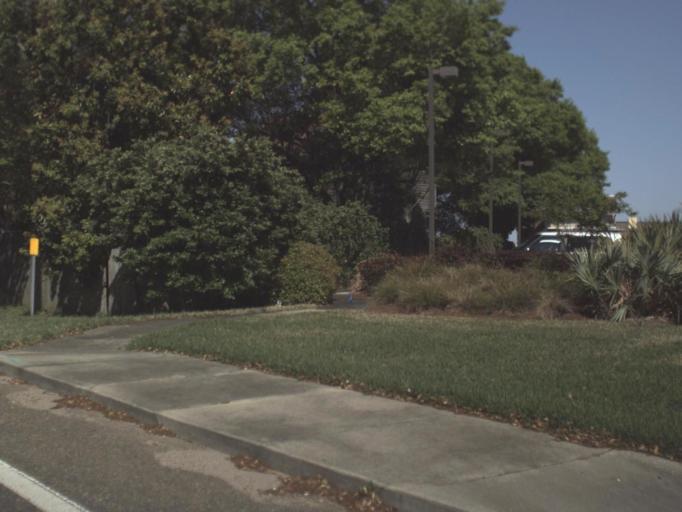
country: US
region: Florida
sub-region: Escambia County
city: East Pensacola Heights
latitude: 30.4343
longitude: -87.1745
